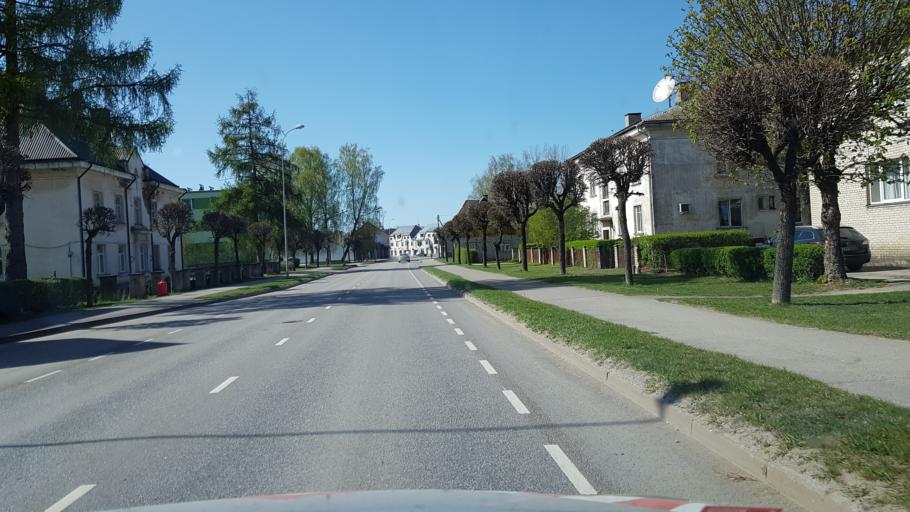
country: EE
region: Valgamaa
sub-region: Torva linn
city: Torva
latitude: 58.0011
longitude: 25.9264
